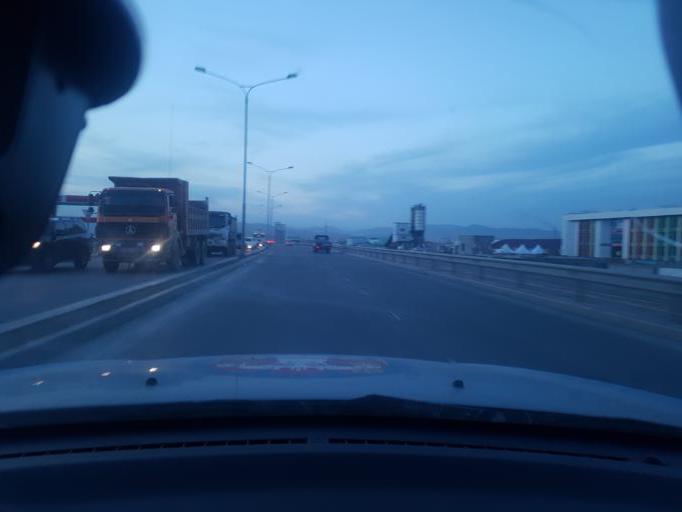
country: MN
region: Ulaanbaatar
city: Ulaanbaatar
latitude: 47.8821
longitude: 106.7852
